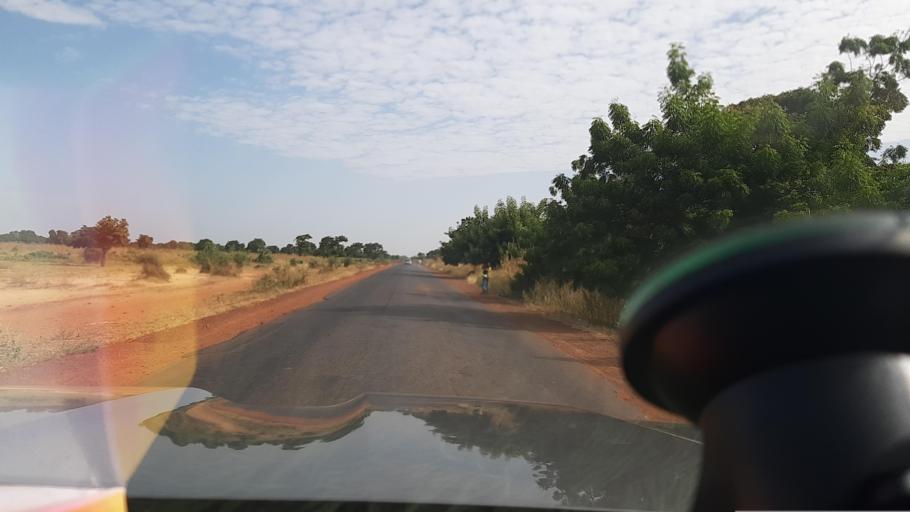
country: ML
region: Segou
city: Segou
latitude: 13.5075
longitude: -6.1454
